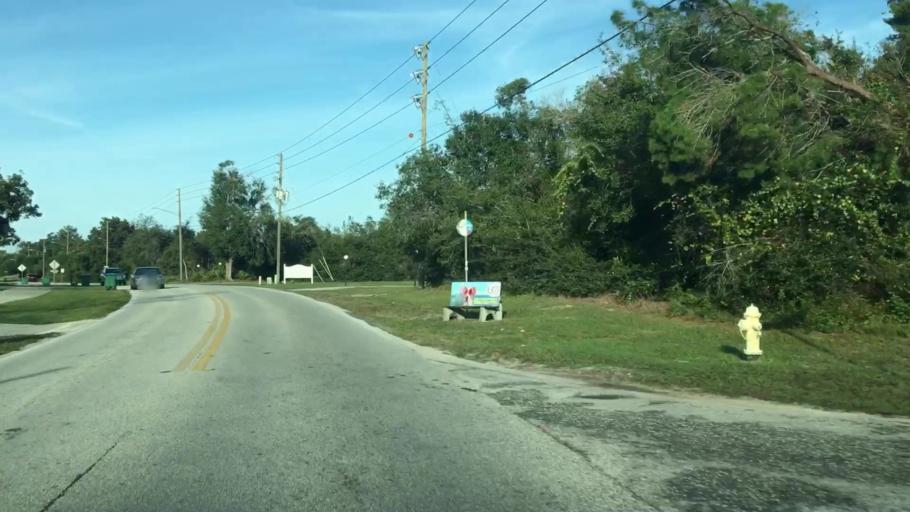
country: US
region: Florida
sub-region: Volusia County
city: Deltona
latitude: 28.9253
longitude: -81.2470
